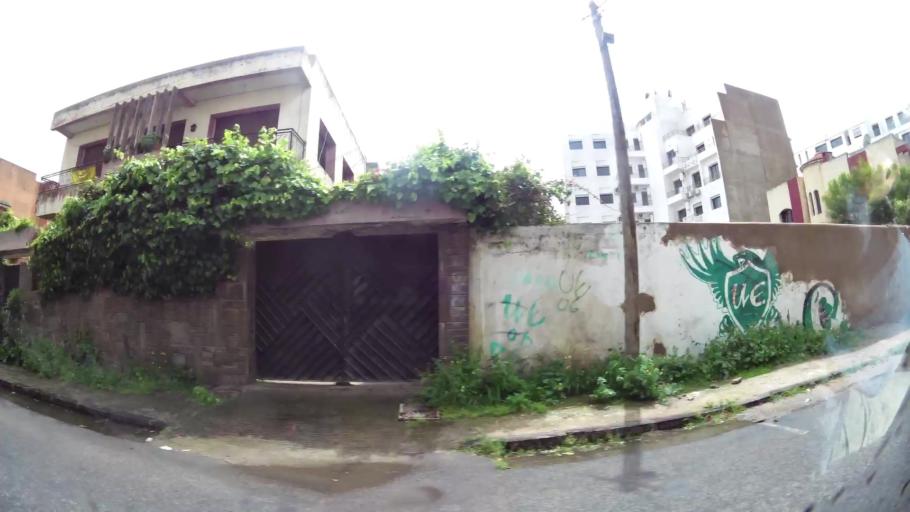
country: MA
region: Grand Casablanca
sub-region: Casablanca
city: Casablanca
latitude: 33.5696
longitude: -7.6160
